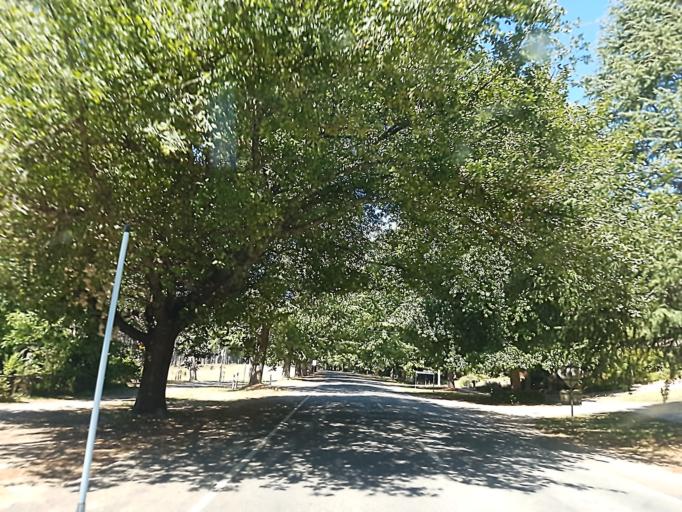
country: AU
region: Victoria
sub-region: Alpine
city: Mount Beauty
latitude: -36.7296
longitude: 146.9802
